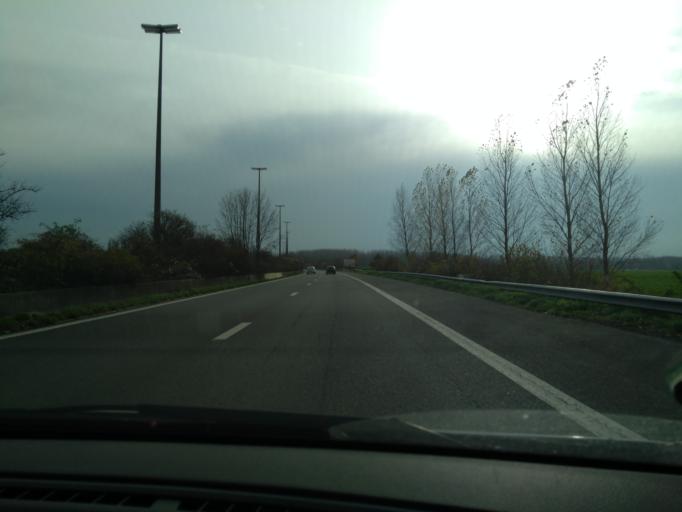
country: BE
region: Wallonia
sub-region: Province du Hainaut
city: Antoing
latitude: 50.5679
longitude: 3.4874
